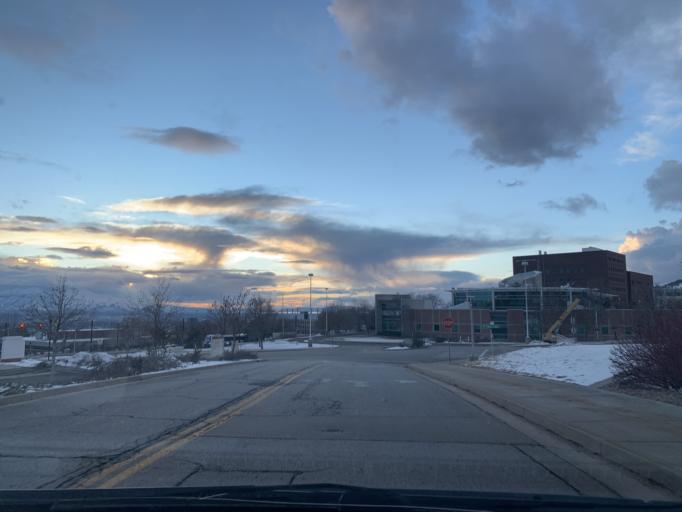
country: US
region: Utah
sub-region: Salt Lake County
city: Salt Lake City
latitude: 40.7682
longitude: -111.8348
